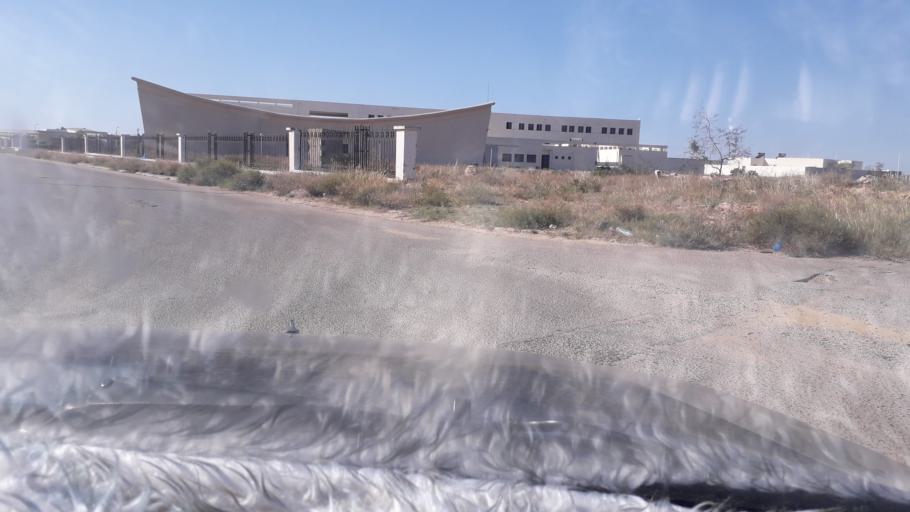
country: TN
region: Safaqis
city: Al Qarmadah
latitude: 34.8400
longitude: 10.7530
